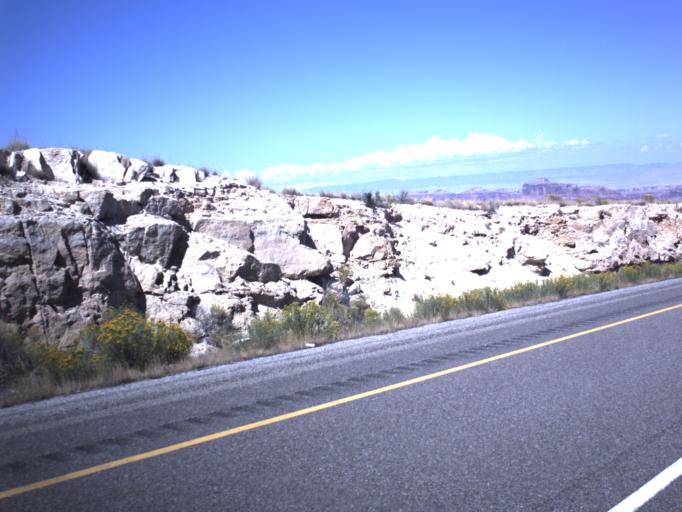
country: US
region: Utah
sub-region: Emery County
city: Castle Dale
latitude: 38.9090
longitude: -110.5276
